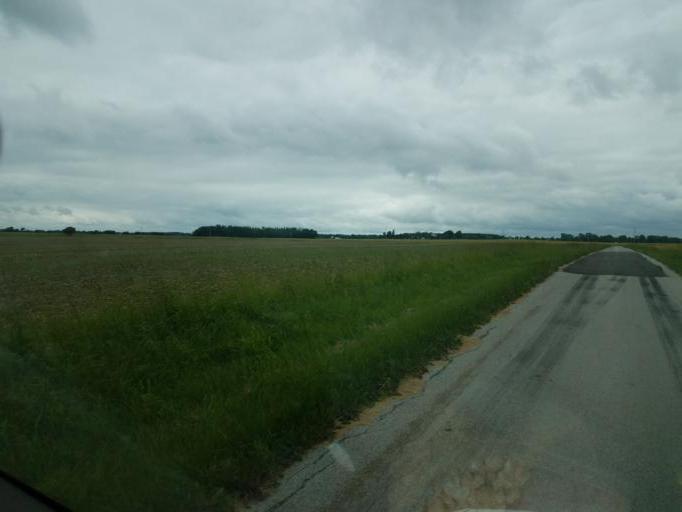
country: US
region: Ohio
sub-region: Morrow County
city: Cardington
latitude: 40.5543
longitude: -82.9146
